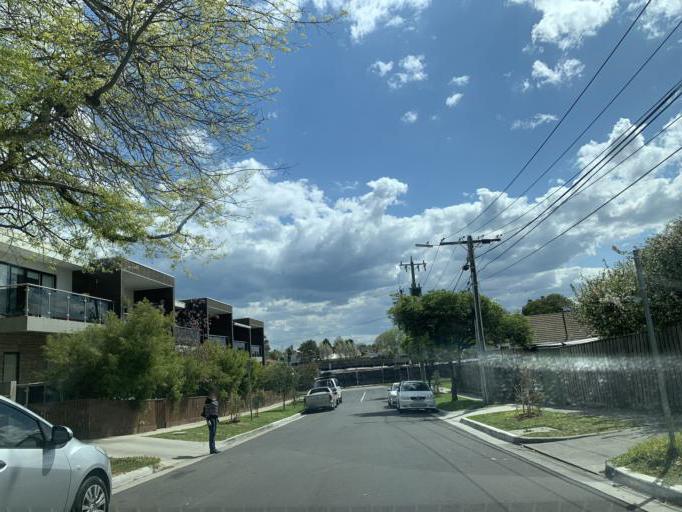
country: AU
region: Victoria
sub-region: Bayside
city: Highett
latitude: -37.9503
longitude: 145.0425
